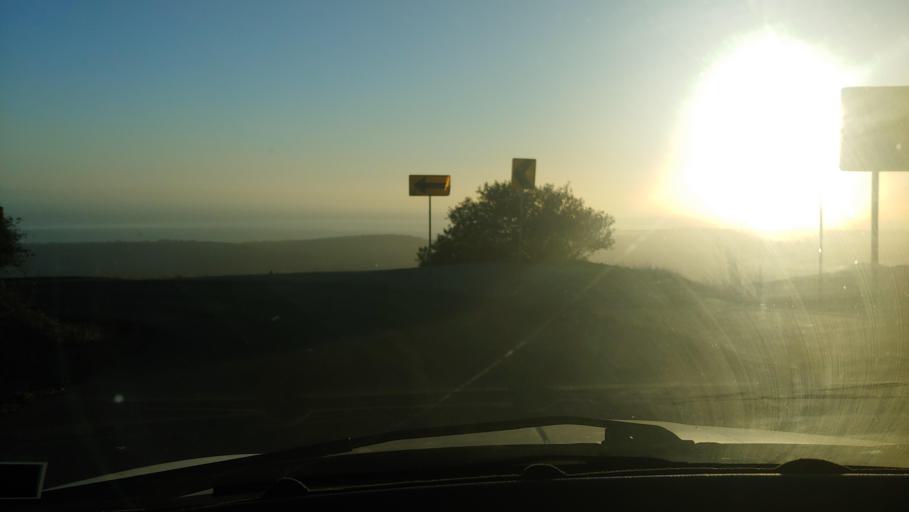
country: US
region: California
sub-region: Santa Barbara County
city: Mission Canyon
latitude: 34.4708
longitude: -119.6798
